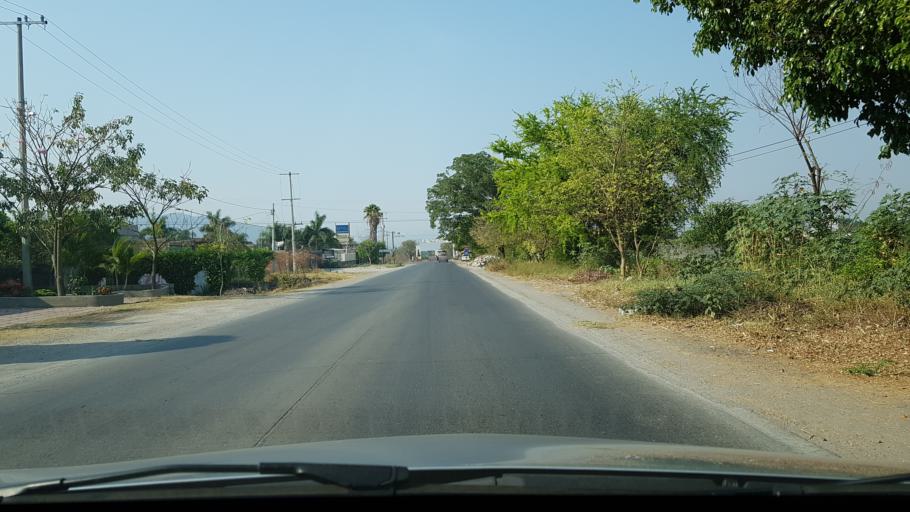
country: MX
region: Morelos
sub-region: Tlaquiltenango
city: Alfredo V. Bonfil (Chacampalco)
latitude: 18.6609
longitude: -99.1501
